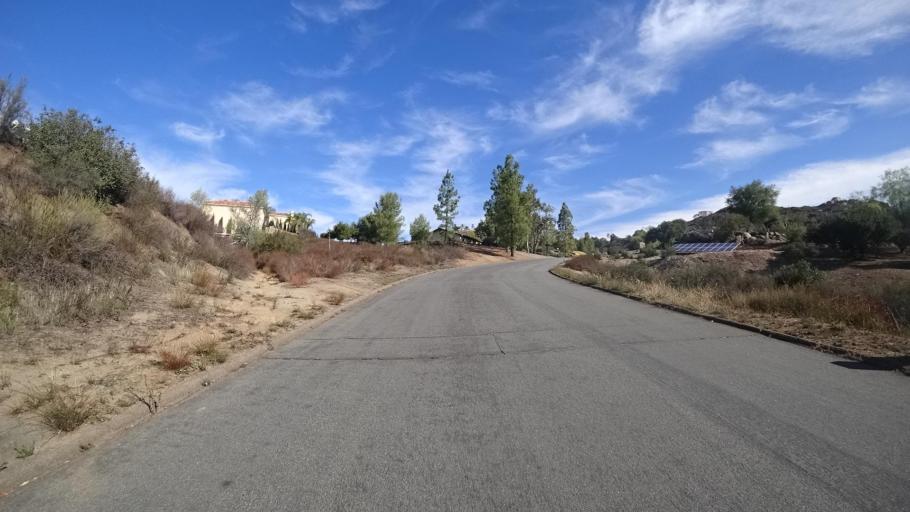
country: US
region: California
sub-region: San Diego County
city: Alpine
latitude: 32.8160
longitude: -116.7404
